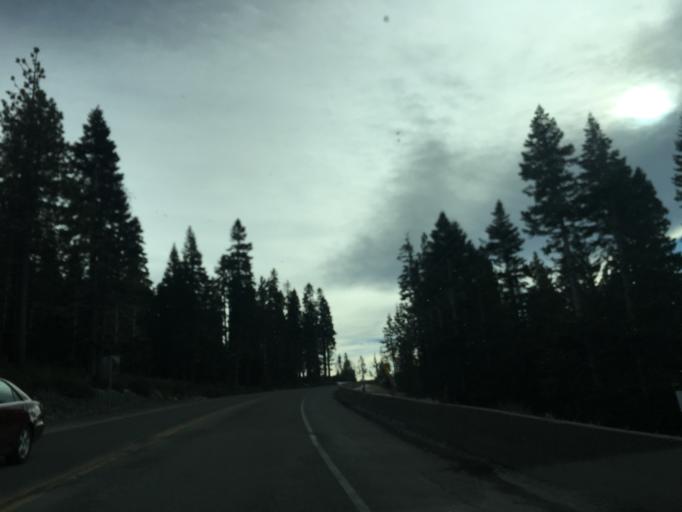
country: US
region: Nevada
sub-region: Washoe County
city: Incline Village
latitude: 39.2658
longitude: -119.9323
